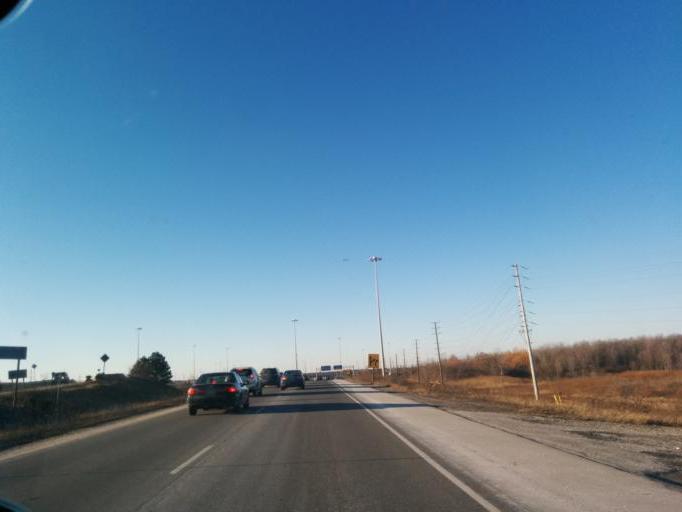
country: CA
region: Ontario
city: Mississauga
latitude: 43.6168
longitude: -79.6300
